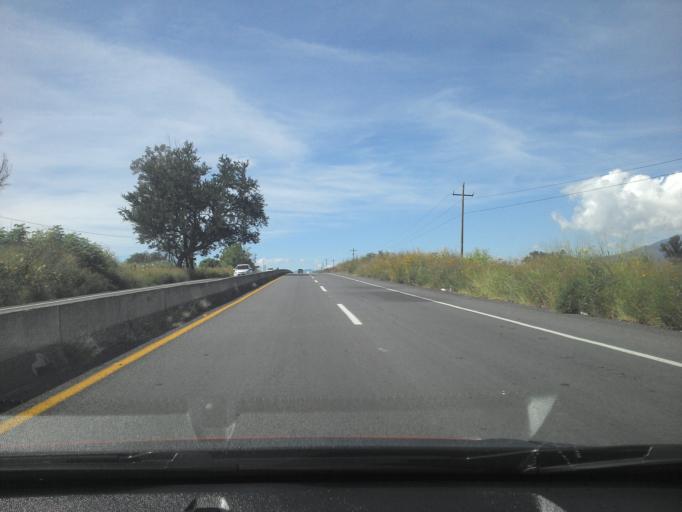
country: MX
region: Jalisco
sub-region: Tala
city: Los Ruisenores
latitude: 20.7156
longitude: -103.6449
